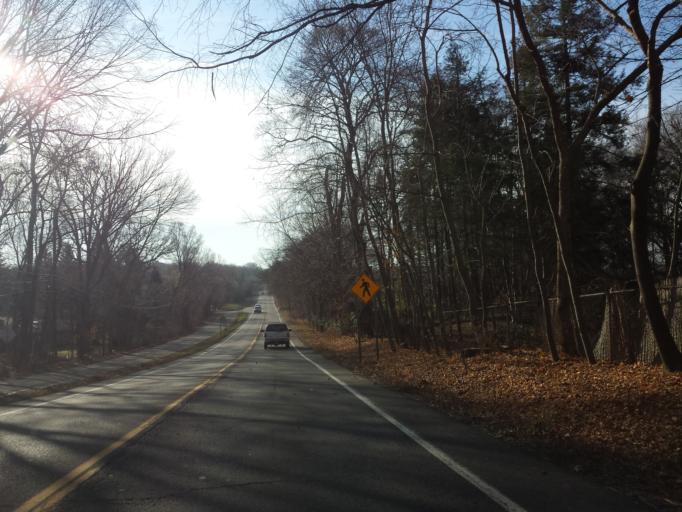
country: US
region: Michigan
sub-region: Oakland County
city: Auburn Hills
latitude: 42.6724
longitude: -83.1937
